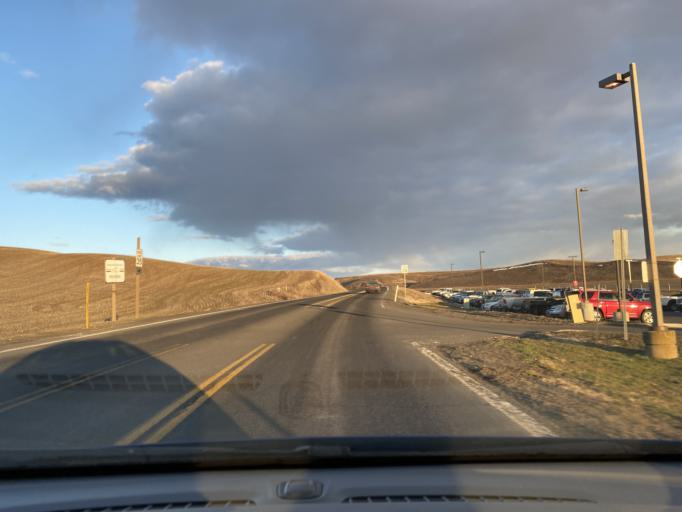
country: US
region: Washington
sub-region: Whitman County
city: Pullman
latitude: 46.7451
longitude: -117.1139
